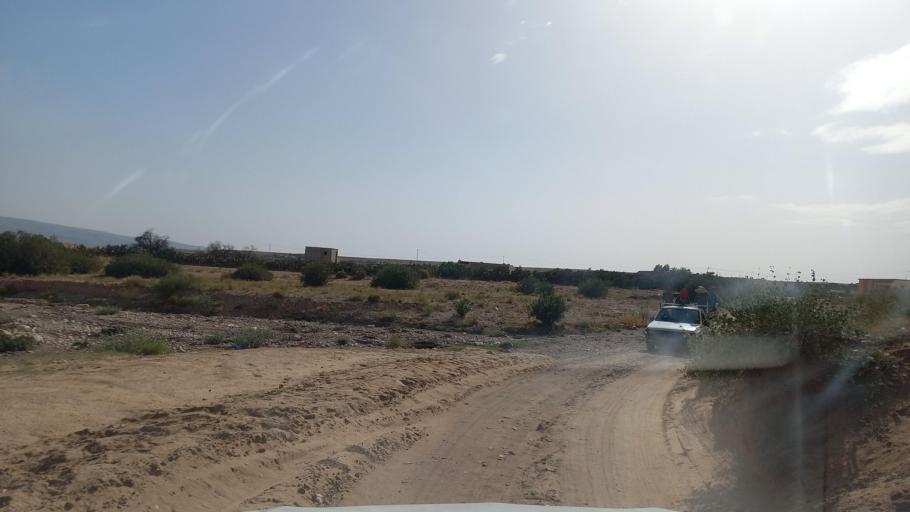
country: TN
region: Al Qasrayn
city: Kasserine
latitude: 35.2719
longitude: 8.9399
